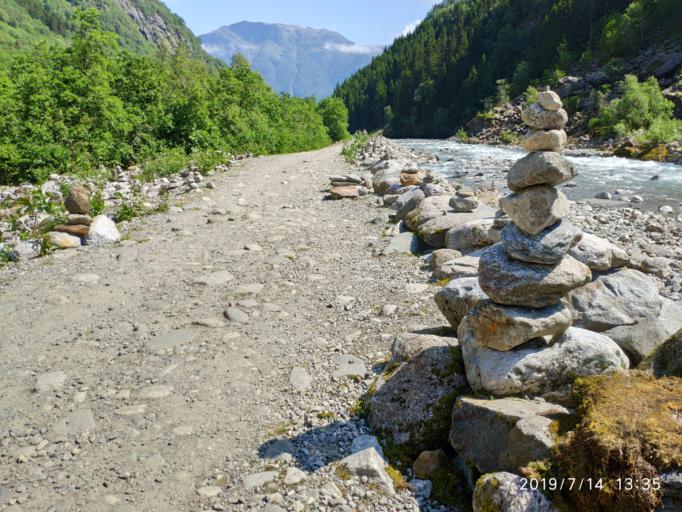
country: NO
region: Hordaland
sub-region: Odda
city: Odda
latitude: 60.0441
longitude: 6.4632
